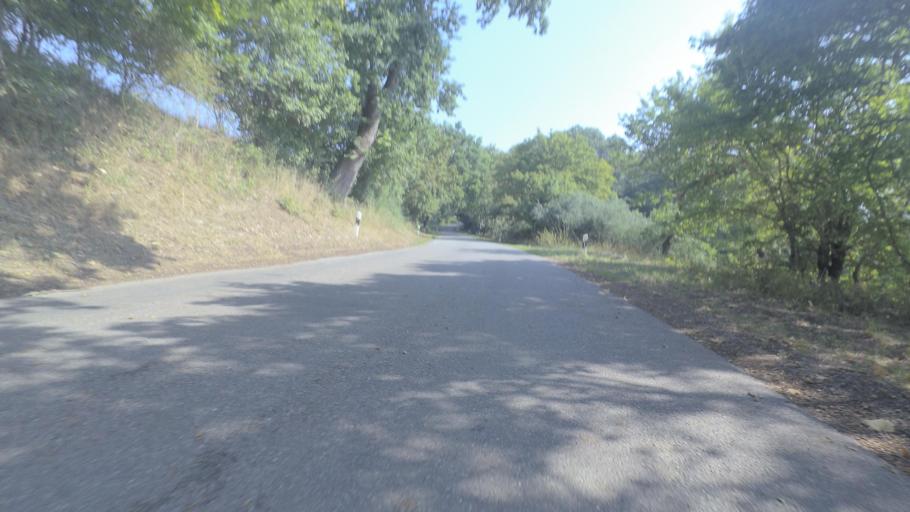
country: DE
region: Mecklenburg-Vorpommern
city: Pampow
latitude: 53.6856
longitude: 12.5836
